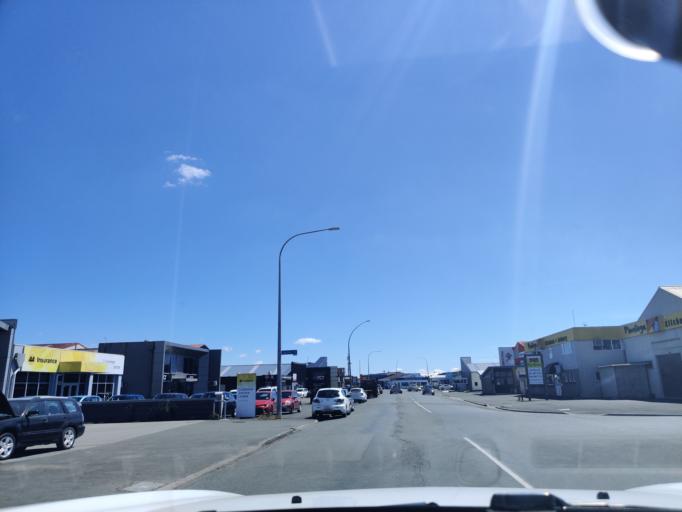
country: NZ
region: Waikato
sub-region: Hamilton City
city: Hamilton
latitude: -37.7965
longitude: 175.2638
